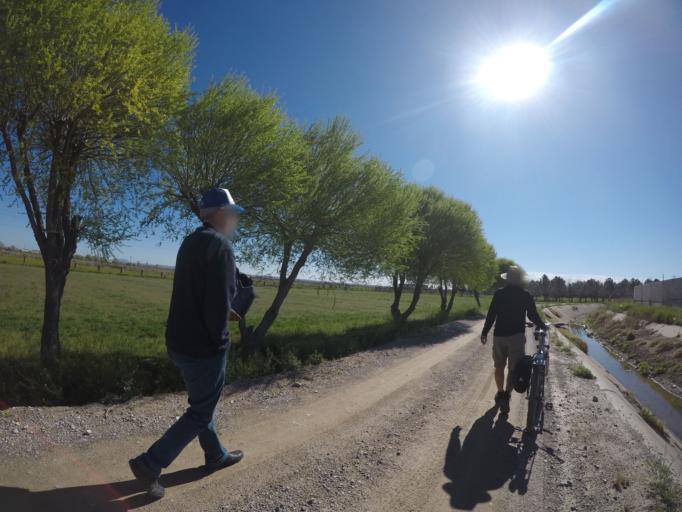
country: US
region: Texas
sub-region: El Paso County
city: Socorro
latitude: 31.6446
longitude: -106.3370
